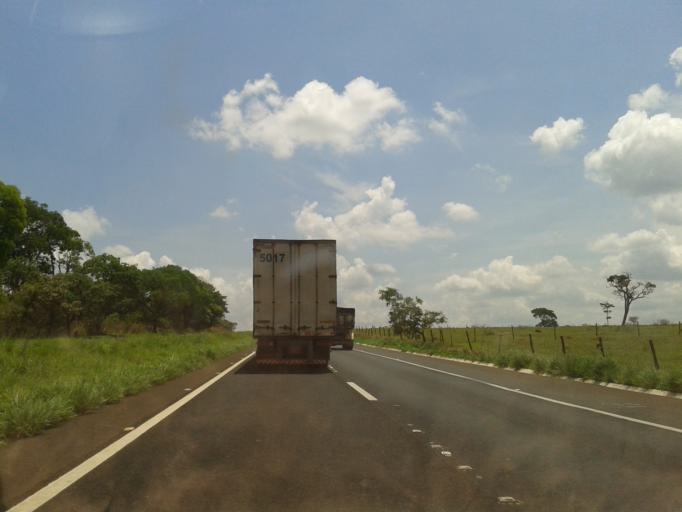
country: BR
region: Minas Gerais
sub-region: Monte Alegre De Minas
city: Monte Alegre de Minas
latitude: -18.8567
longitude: -48.7749
